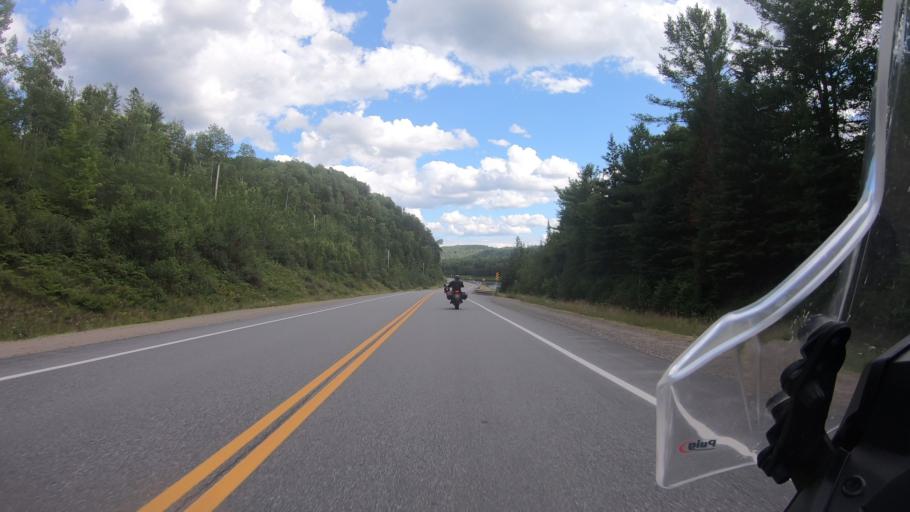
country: CA
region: Quebec
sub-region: Mauricie
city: Saint-Tite
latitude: 47.0020
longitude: -72.9250
